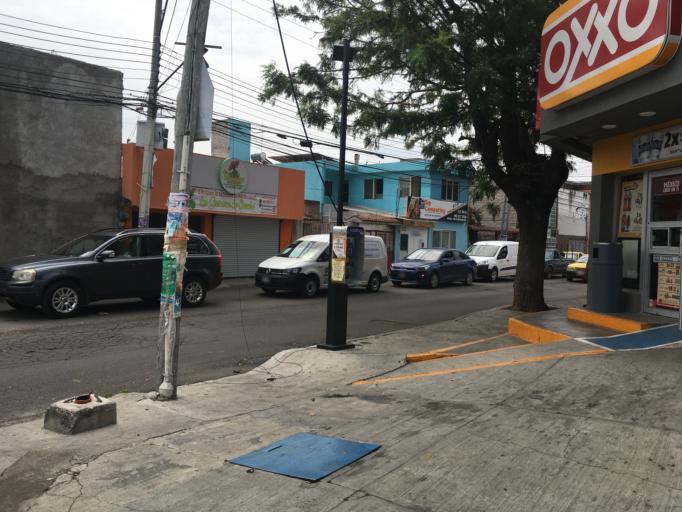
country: MX
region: Queretaro
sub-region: Queretaro
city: Santiago de Queretaro
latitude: 20.6129
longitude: -100.3999
